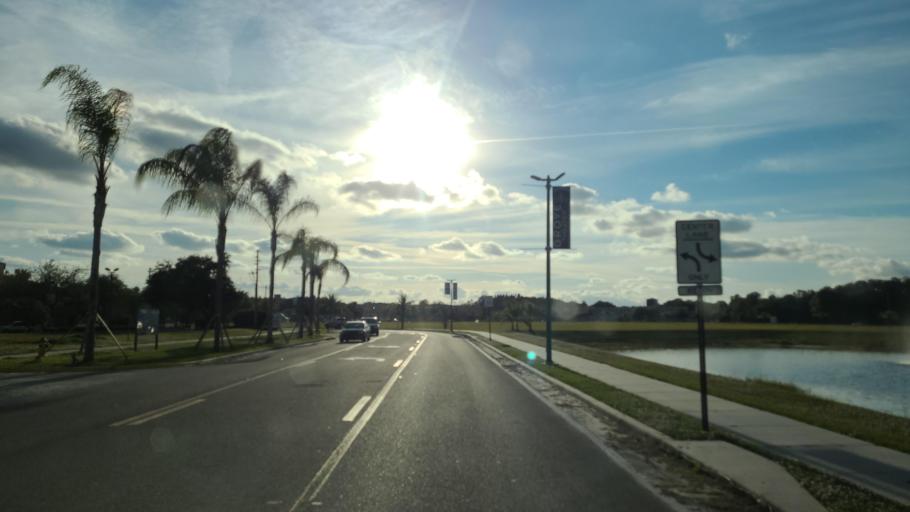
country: US
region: Florida
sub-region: Pasco County
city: Wesley Chapel
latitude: 28.2412
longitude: -82.3533
